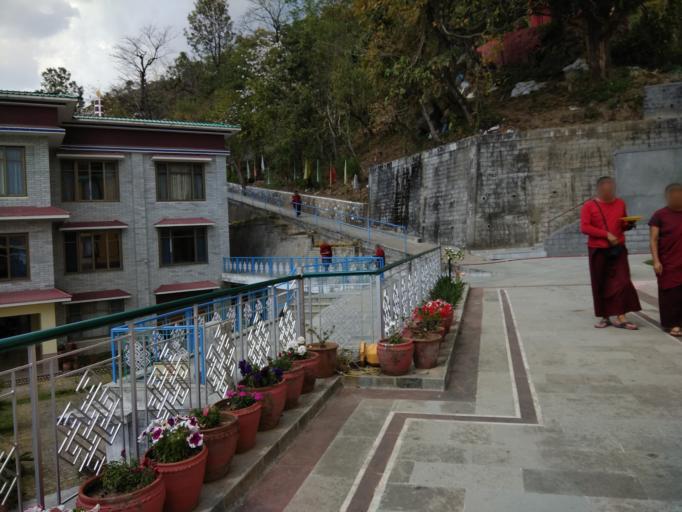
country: IN
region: Himachal Pradesh
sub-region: Kangra
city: Palampur
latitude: 32.0752
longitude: 76.6247
